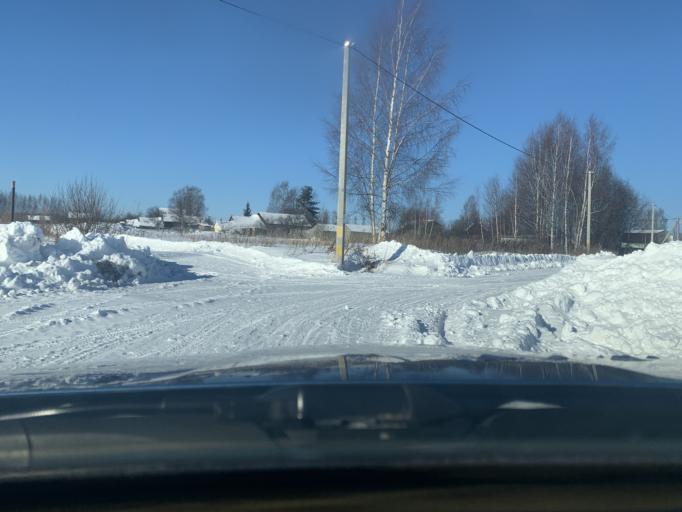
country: RU
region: Jaroslavl
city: Tunoshna
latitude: 57.6501
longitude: 40.0680
